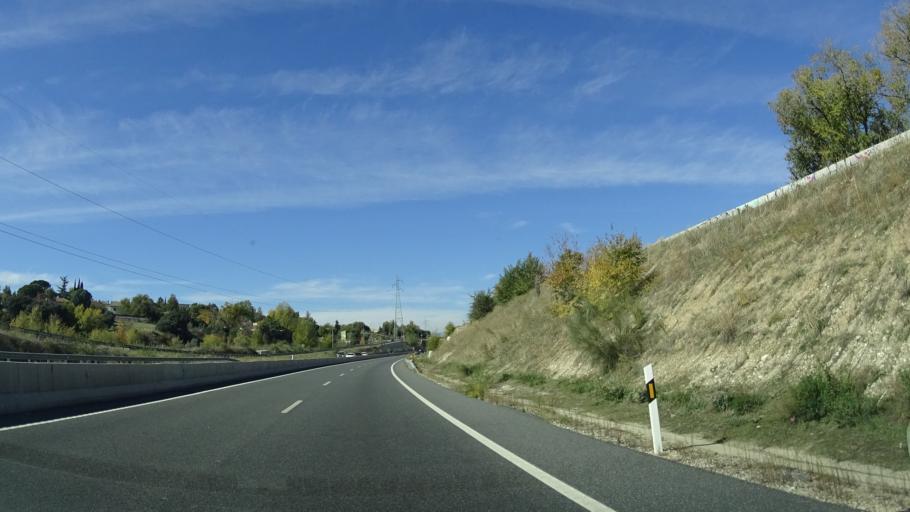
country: ES
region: Madrid
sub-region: Provincia de Madrid
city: Villanueva del Pardillo
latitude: 40.4853
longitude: -3.9416
